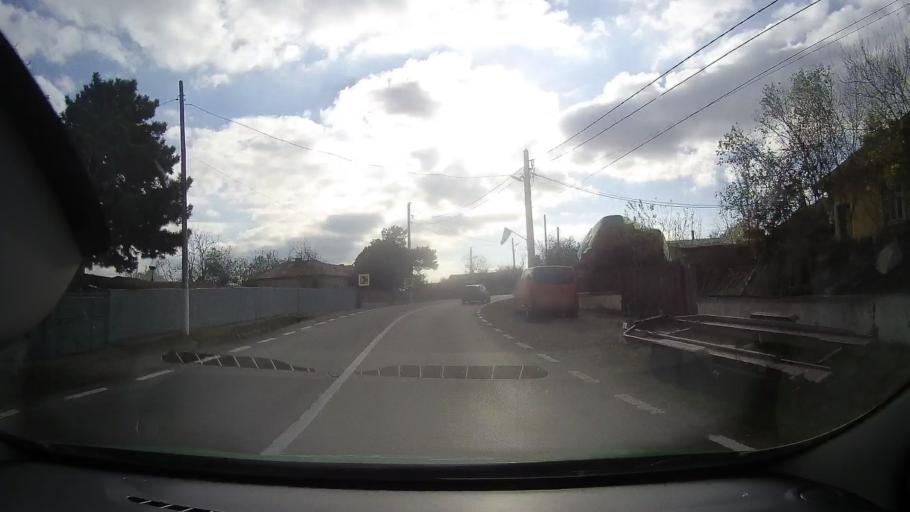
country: RO
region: Tulcea
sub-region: Comuna Topolog
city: Topolog
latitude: 44.8742
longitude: 28.3733
